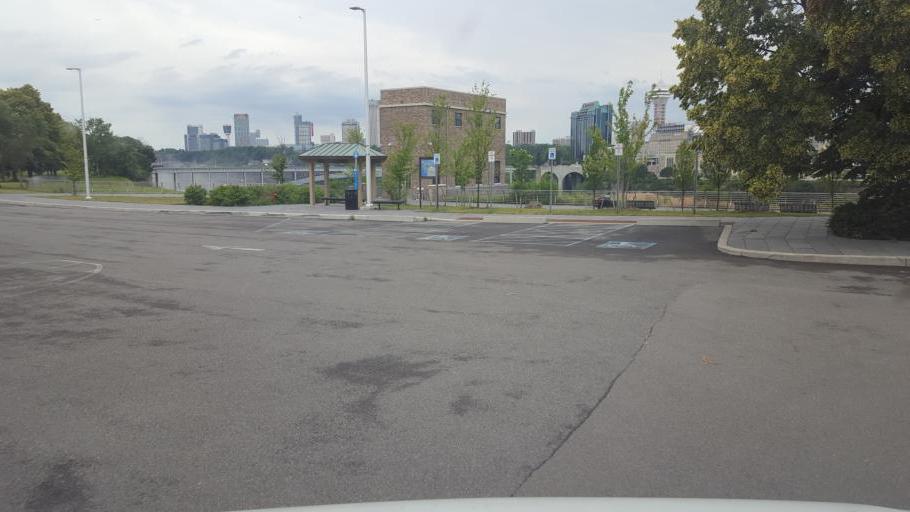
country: US
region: New York
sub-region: Niagara County
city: Niagara Falls
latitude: 43.0929
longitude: -79.0620
